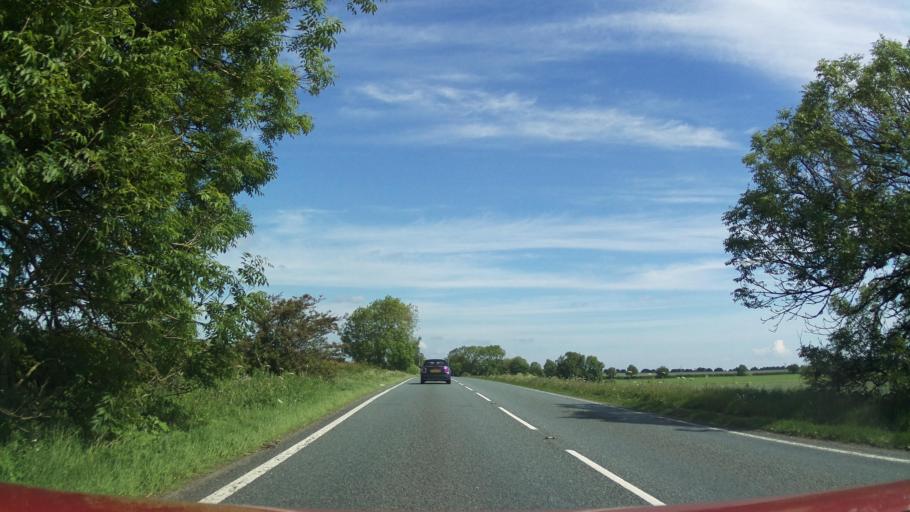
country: GB
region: England
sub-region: Lincolnshire
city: Burton
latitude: 53.2790
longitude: -0.5401
